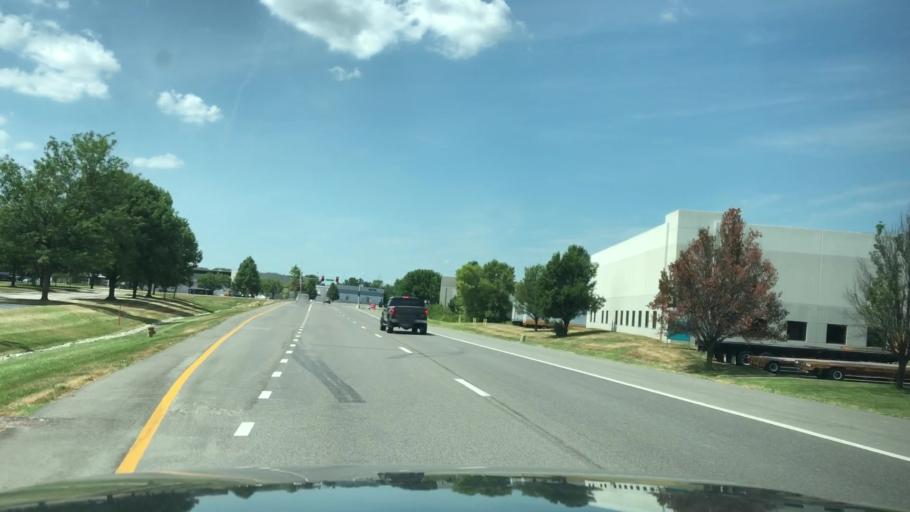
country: US
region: Missouri
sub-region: Saint Charles County
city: Saint Charles
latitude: 38.7713
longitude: -90.4581
